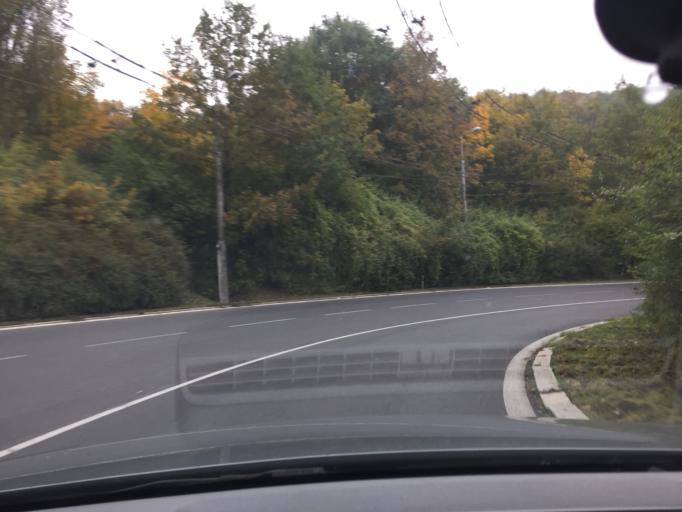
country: CZ
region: Ustecky
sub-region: Okres Usti nad Labem
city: Usti nad Labem
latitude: 50.6680
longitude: 14.0451
